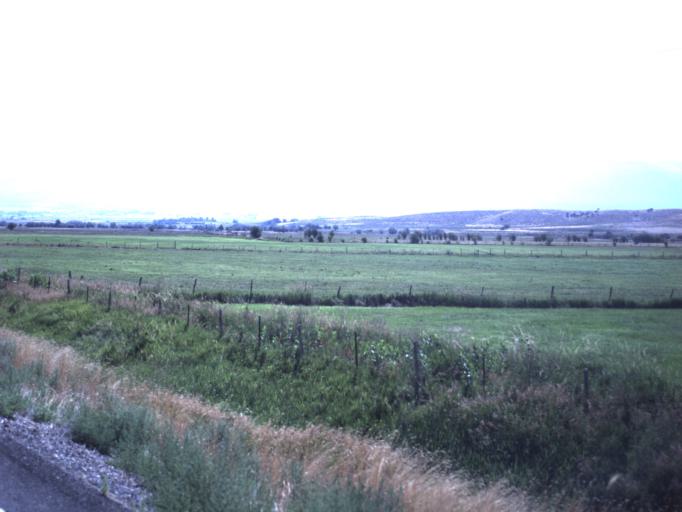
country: US
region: Utah
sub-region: Sanpete County
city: Moroni
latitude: 39.5270
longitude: -111.5499
